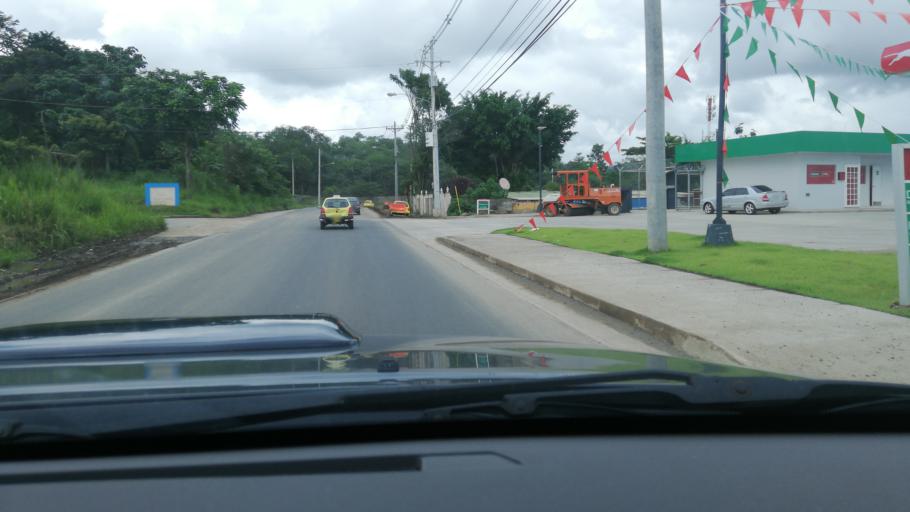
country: PA
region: Panama
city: San Miguelito
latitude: 9.0897
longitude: -79.4521
